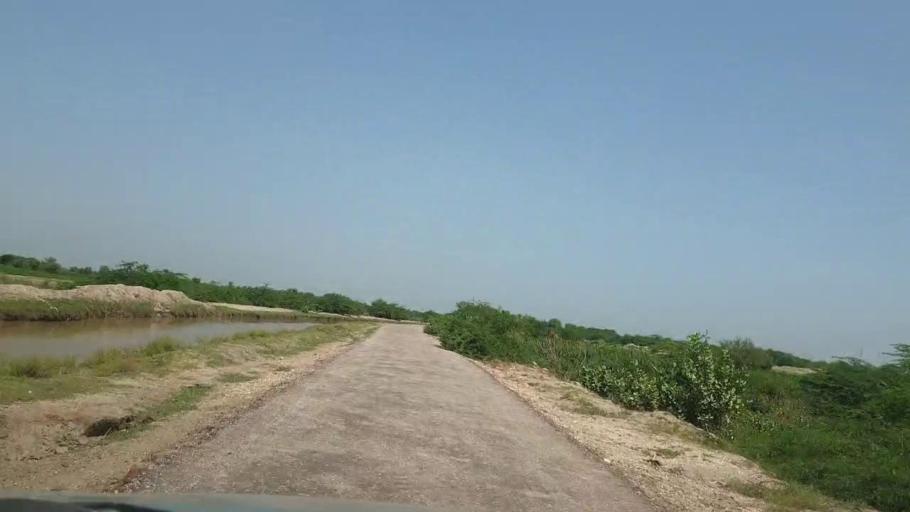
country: PK
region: Sindh
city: Rohri
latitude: 27.6252
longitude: 69.0978
